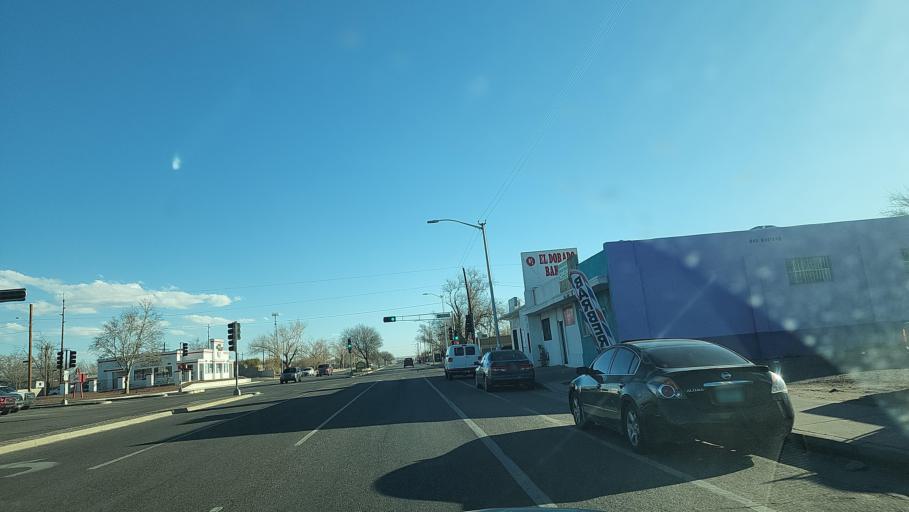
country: US
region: New Mexico
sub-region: Bernalillo County
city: Albuquerque
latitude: 35.0615
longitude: -106.6454
